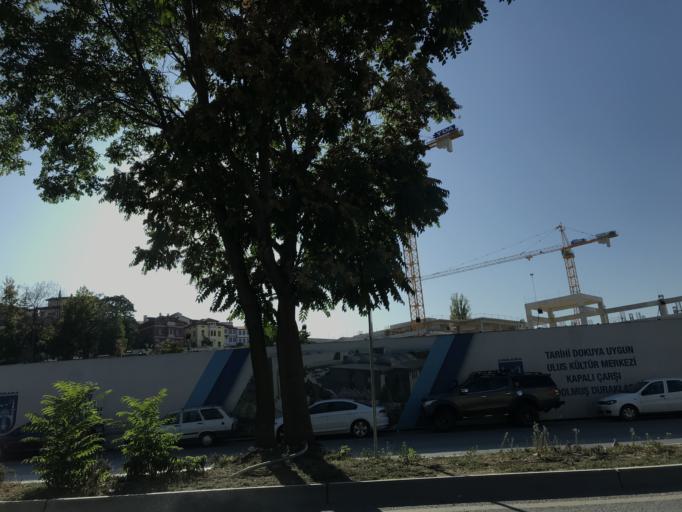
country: TR
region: Ankara
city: Ankara
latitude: 39.9456
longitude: 32.8608
